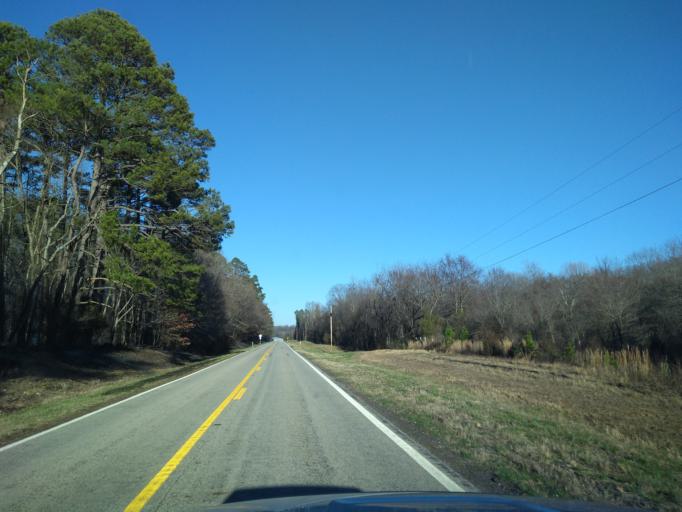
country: US
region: Arkansas
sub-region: Washington County
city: Farmington
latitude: 36.0935
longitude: -94.3613
